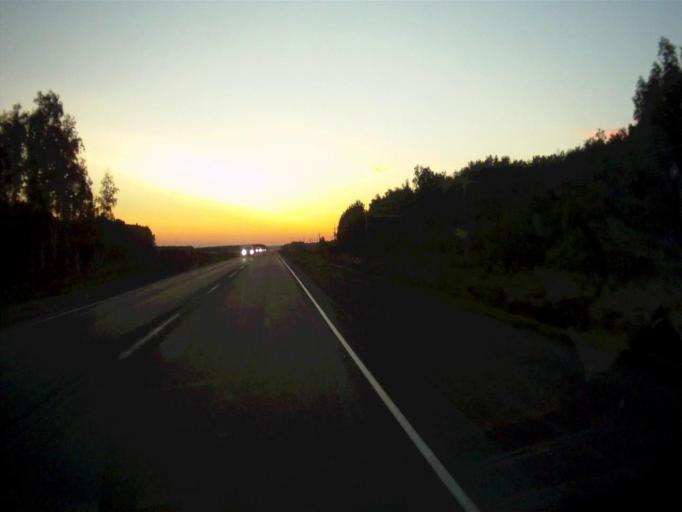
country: RU
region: Chelyabinsk
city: Poletayevo
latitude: 55.2133
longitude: 61.0656
